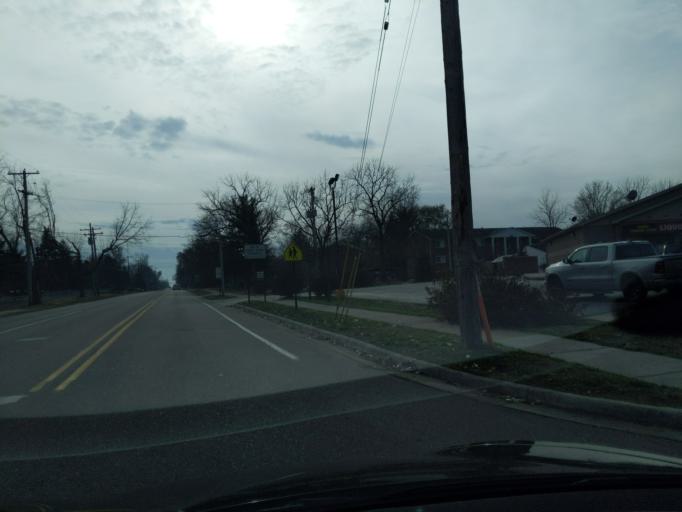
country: US
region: Michigan
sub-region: Ingham County
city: Holt
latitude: 42.6546
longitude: -84.5235
